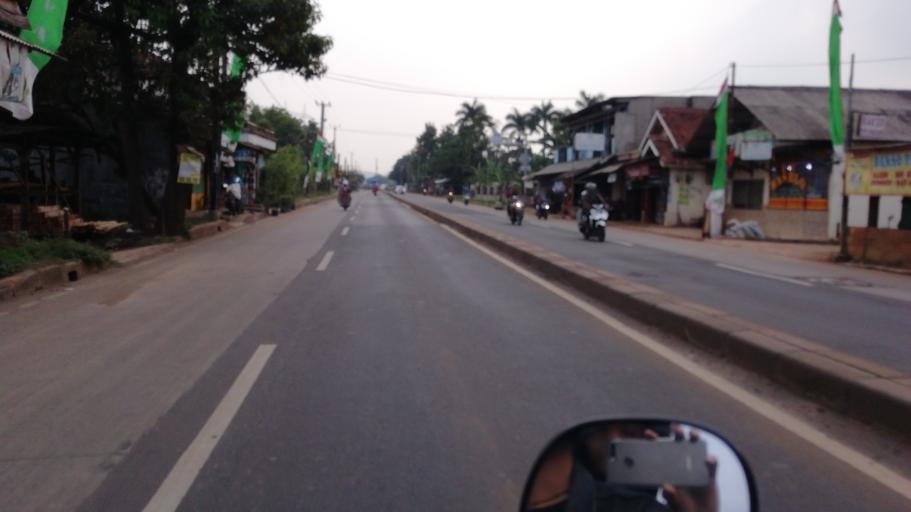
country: ID
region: West Java
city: Parung
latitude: -6.4666
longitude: 106.7292
